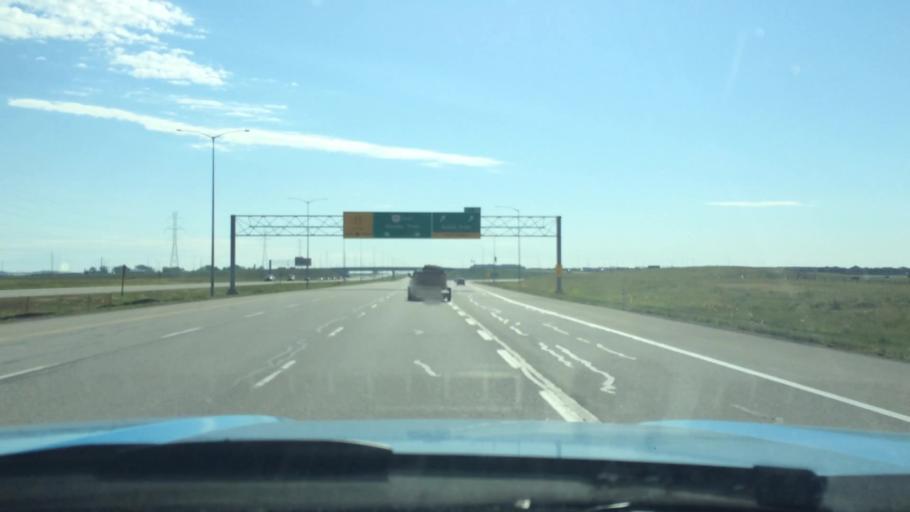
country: CA
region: Alberta
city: Airdrie
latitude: 51.1754
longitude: -113.9814
